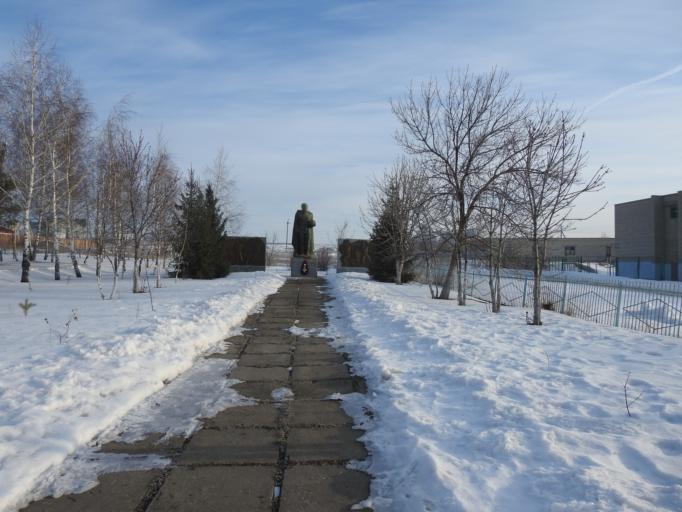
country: RU
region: Saratov
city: Krasnyy Oktyabr'
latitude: 51.4969
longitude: 45.7165
